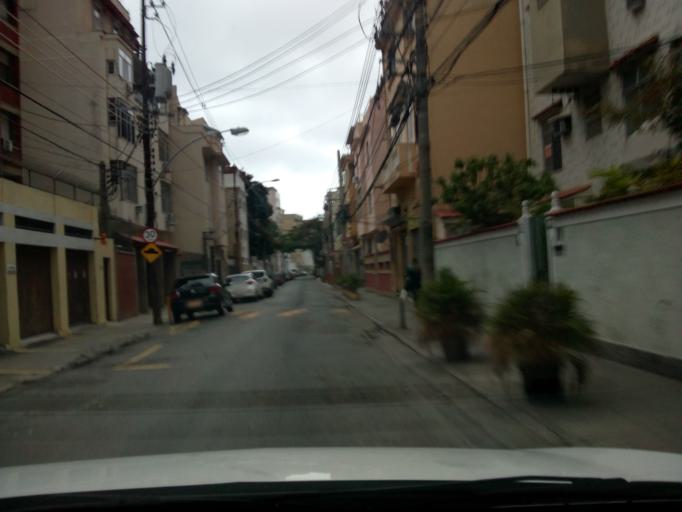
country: BR
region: Rio de Janeiro
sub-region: Rio De Janeiro
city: Rio de Janeiro
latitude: -22.9501
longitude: -43.1670
